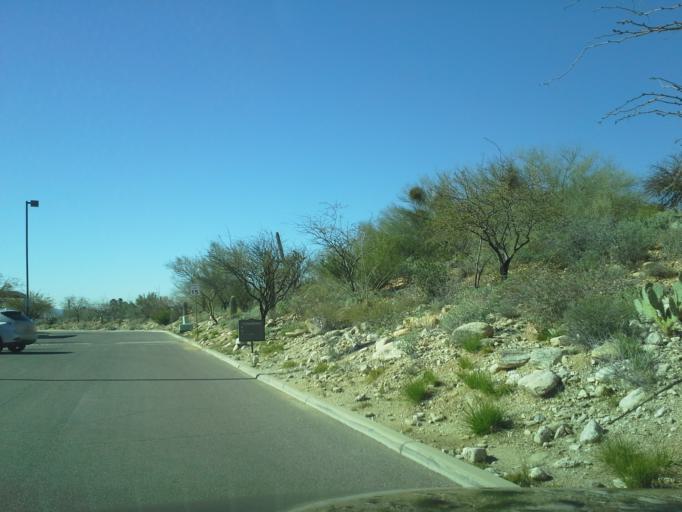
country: US
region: Arizona
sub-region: Pima County
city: Catalina Foothills
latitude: 32.3261
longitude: -110.9296
